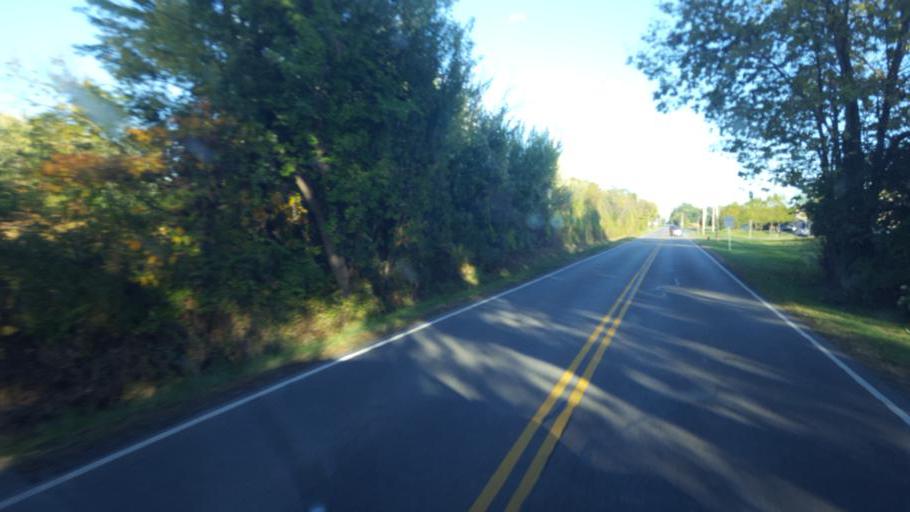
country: US
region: Ohio
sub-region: Franklin County
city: New Albany
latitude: 40.0180
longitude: -82.7684
